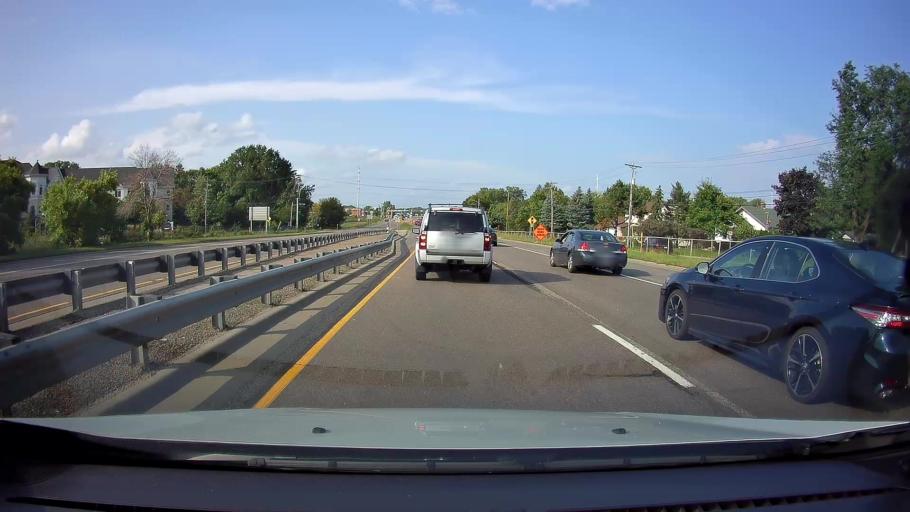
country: US
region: Minnesota
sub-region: Ramsey County
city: Roseville
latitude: 45.0171
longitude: -93.1668
